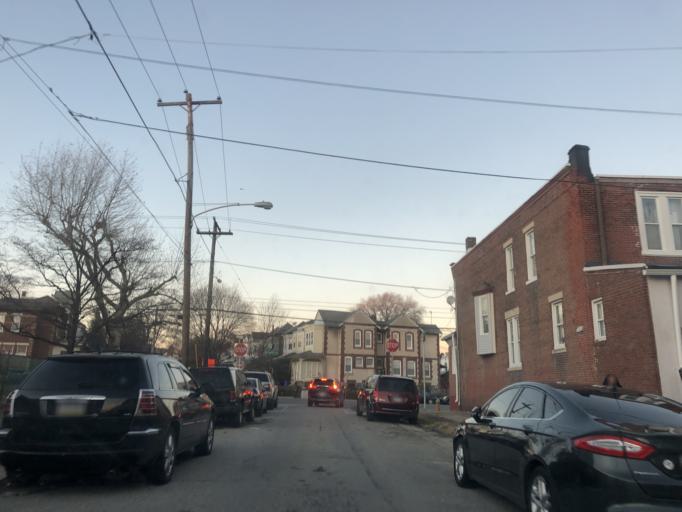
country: US
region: Pennsylvania
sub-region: Delaware County
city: Millbourne
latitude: 39.9716
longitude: -75.2460
